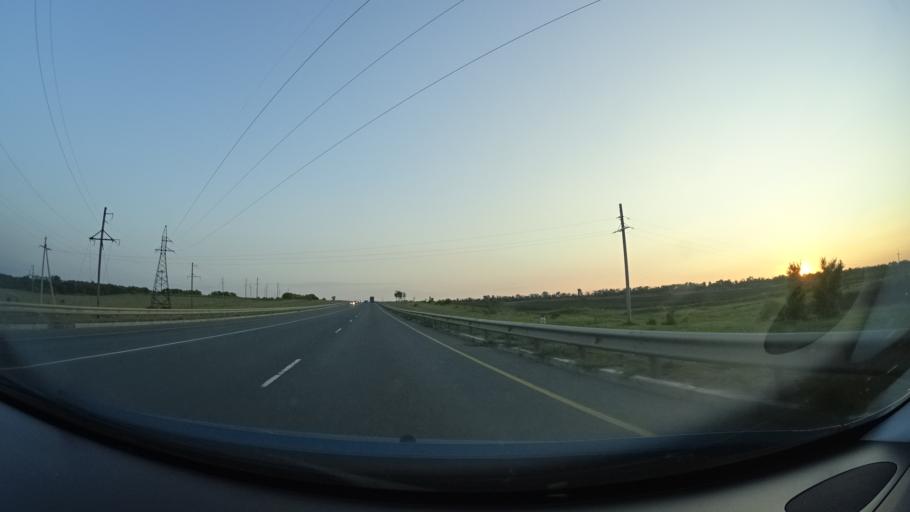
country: RU
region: Samara
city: Sukhodol
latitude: 53.8645
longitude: 51.1846
